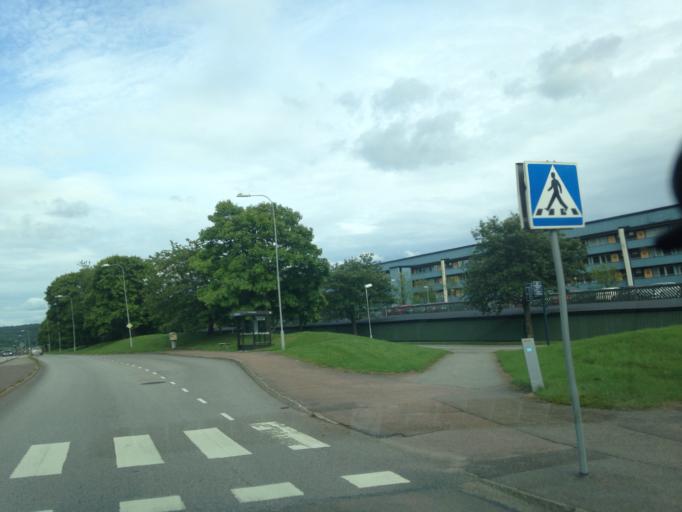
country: SE
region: Vaestra Goetaland
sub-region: Goteborg
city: Goeteborg
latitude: 57.7551
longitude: 11.9719
